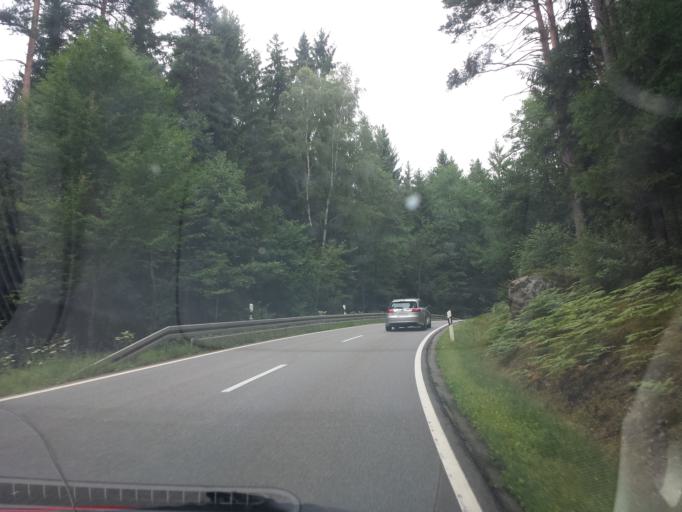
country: DE
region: Bavaria
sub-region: Lower Bavaria
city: Viechtach
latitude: 49.1101
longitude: 12.8835
